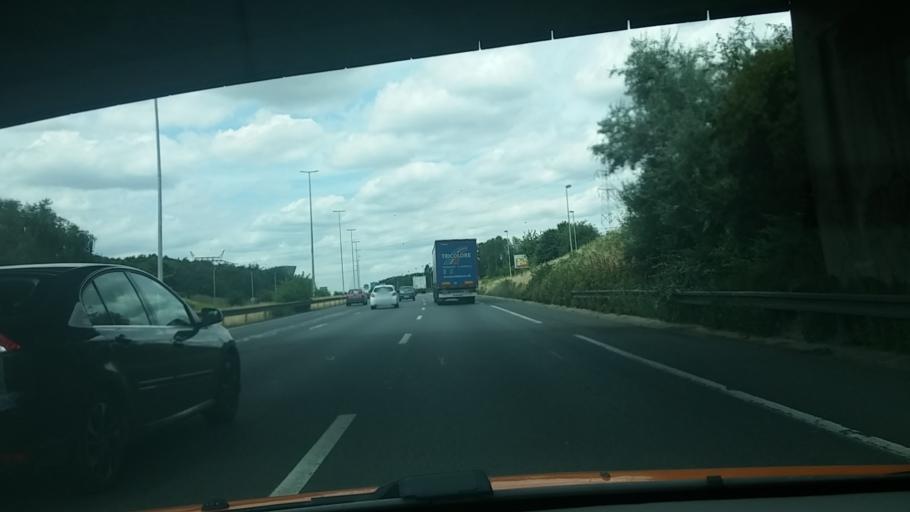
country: FR
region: Ile-de-France
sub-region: Departement de Seine-Saint-Denis
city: Villepinte
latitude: 48.9653
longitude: 2.5182
